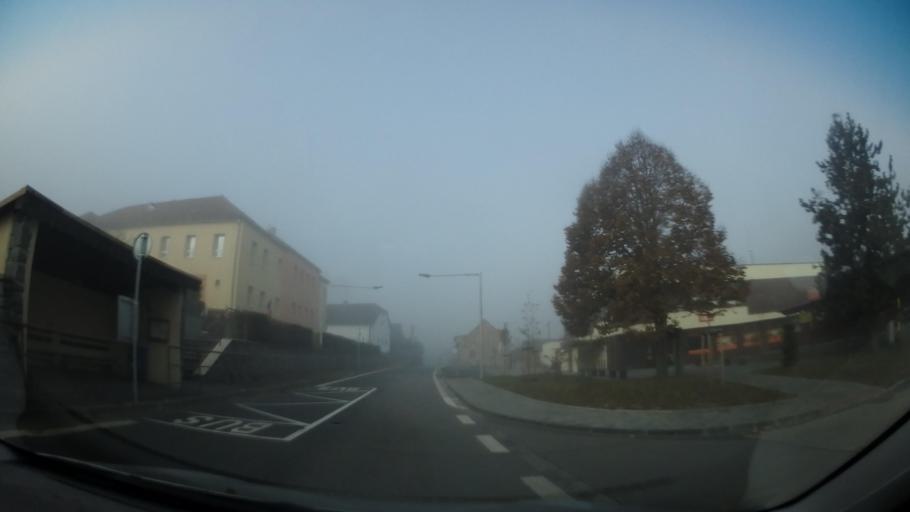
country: CZ
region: Vysocina
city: Krizanov
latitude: 49.4411
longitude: 16.1926
